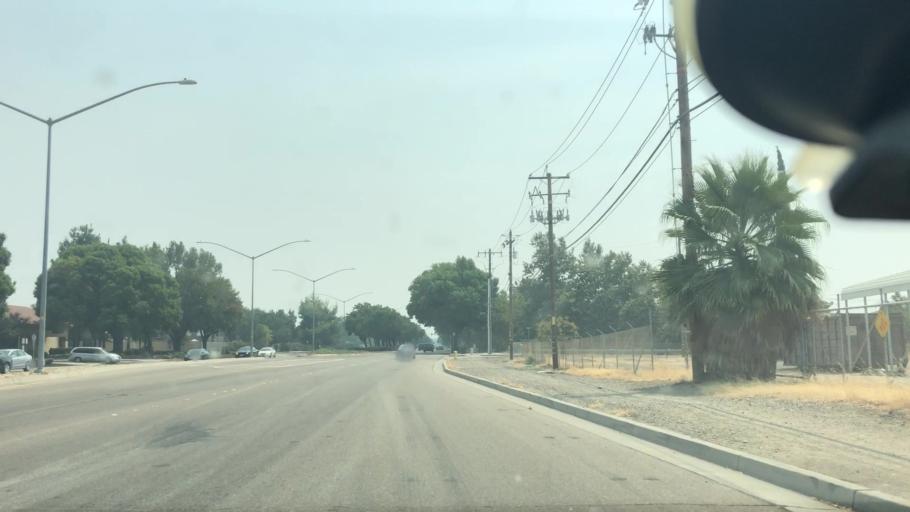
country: US
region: California
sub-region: San Joaquin County
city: Tracy
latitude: 37.7385
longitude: -121.4533
